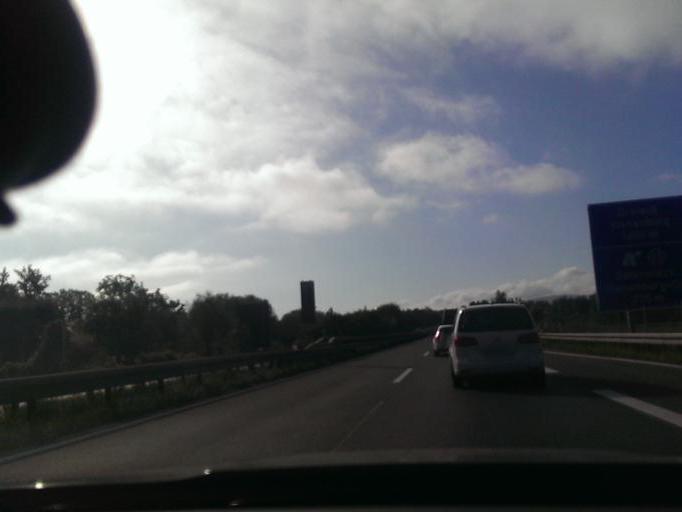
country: DE
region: Lower Saxony
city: Vienenburg
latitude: 51.9556
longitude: 10.5811
